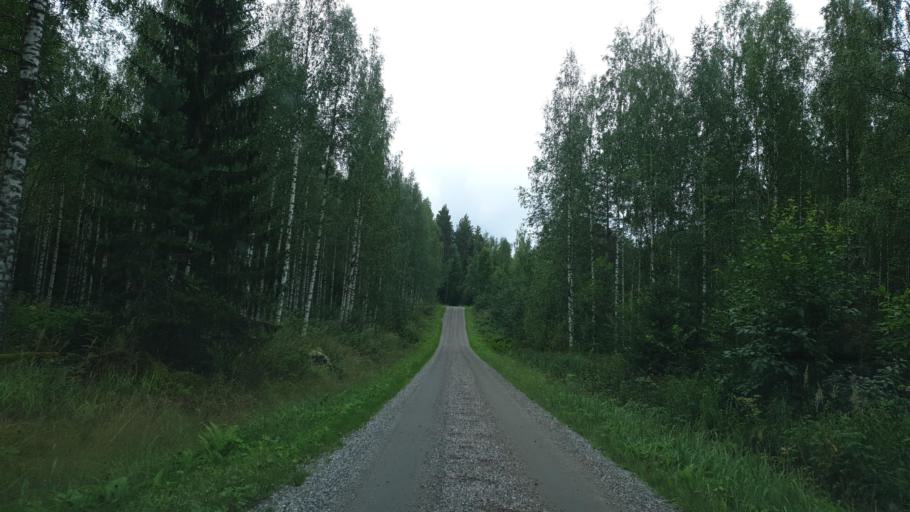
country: FI
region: Northern Savo
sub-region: Kuopio
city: Nilsiae
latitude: 63.2416
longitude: 28.2549
